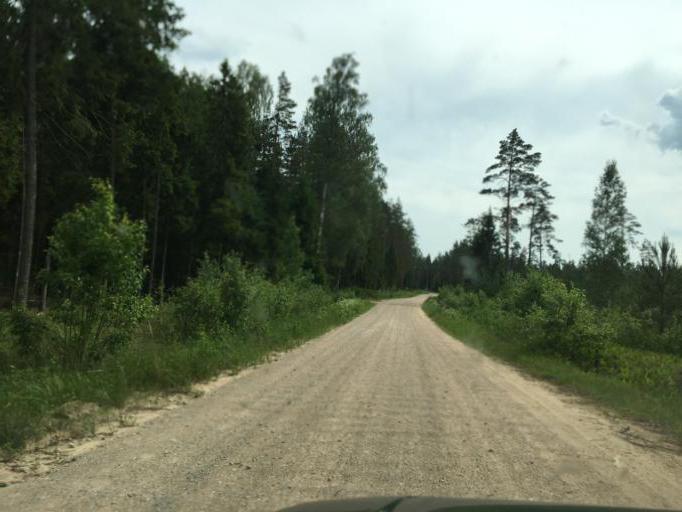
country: LV
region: Rugaju
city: Rugaji
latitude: 56.7730
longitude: 27.1046
